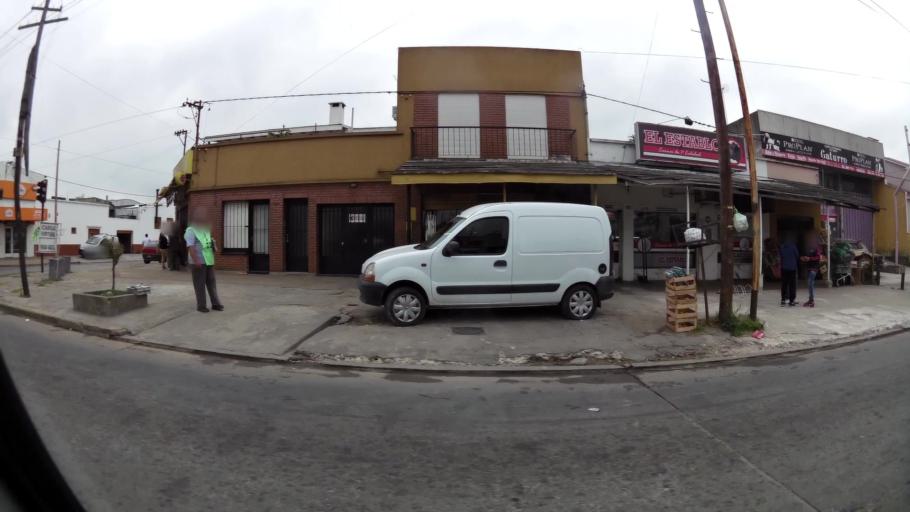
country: AR
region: Buenos Aires
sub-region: Partido de La Plata
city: La Plata
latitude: -34.8865
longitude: -57.9784
